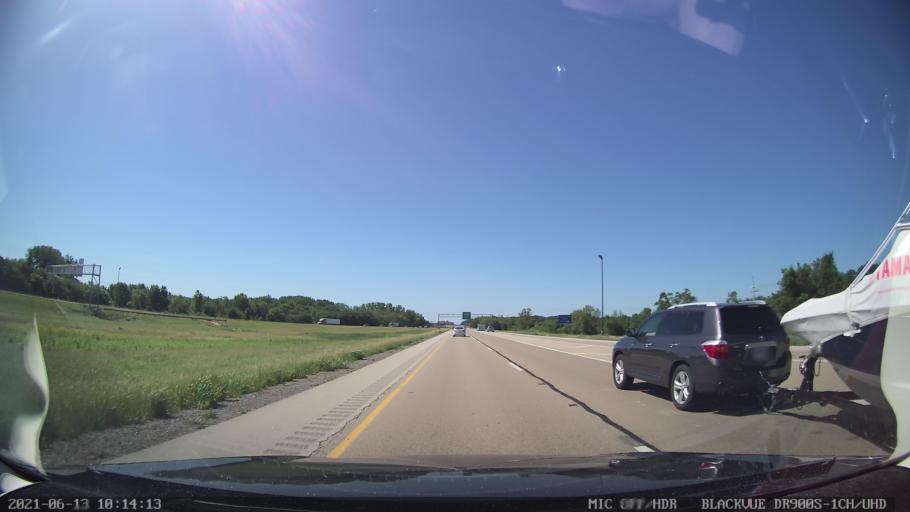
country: US
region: Illinois
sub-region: Logan County
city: Lincoln
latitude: 40.1736
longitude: -89.4176
